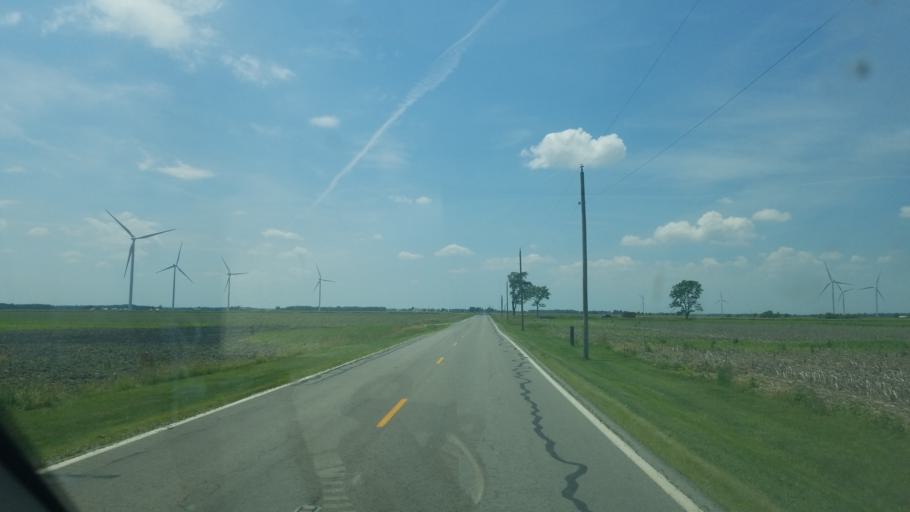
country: US
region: Ohio
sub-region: Hardin County
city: Ada
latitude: 40.7763
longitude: -83.7136
